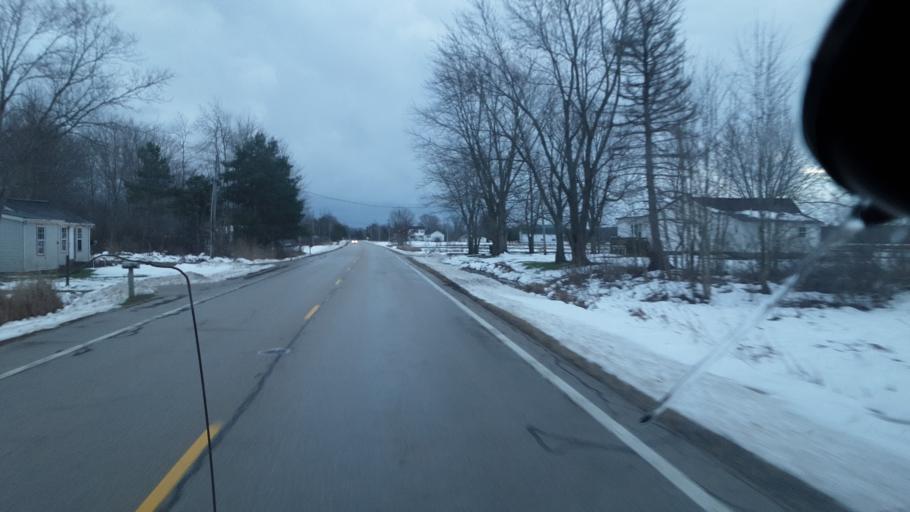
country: US
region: Ohio
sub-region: Ashtabula County
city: Jefferson
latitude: 41.6957
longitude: -80.7004
